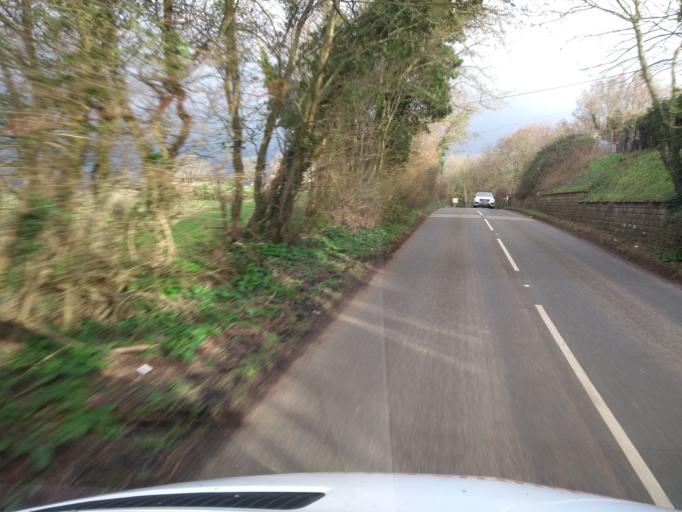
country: GB
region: England
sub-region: Somerset
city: Bruton
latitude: 51.0962
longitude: -2.4659
